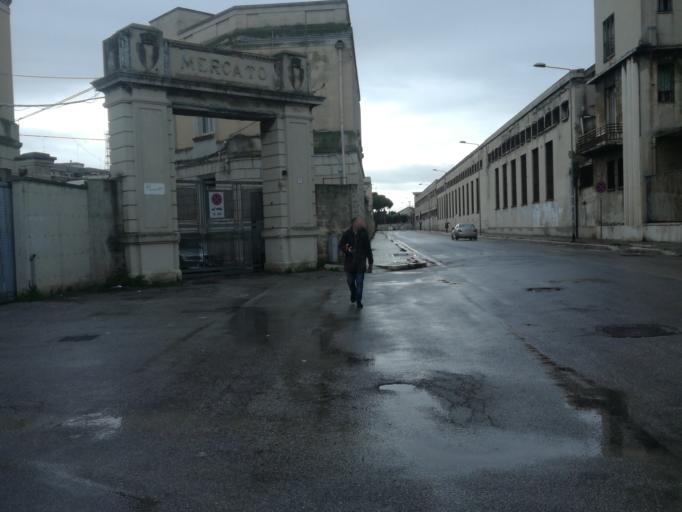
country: IT
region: Apulia
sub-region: Provincia di Bari
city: Bari
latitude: 41.1301
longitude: 16.8443
